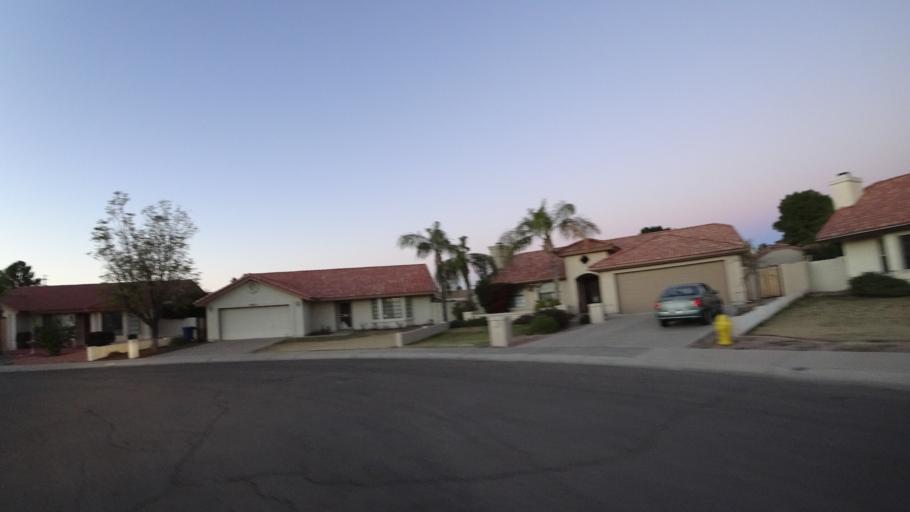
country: US
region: Arizona
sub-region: Maricopa County
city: Tempe Junction
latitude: 33.4153
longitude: -111.9594
